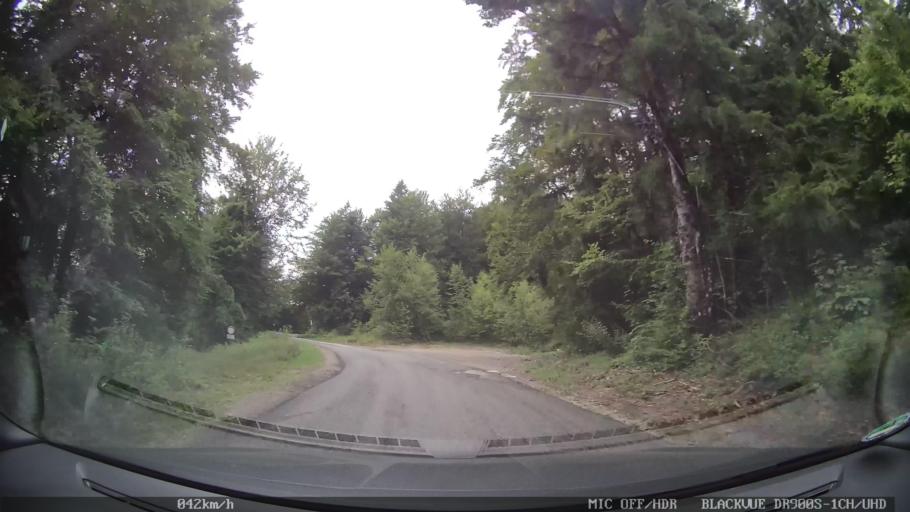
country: HR
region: Licko-Senjska
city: Jezerce
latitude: 44.9295
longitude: 15.5548
